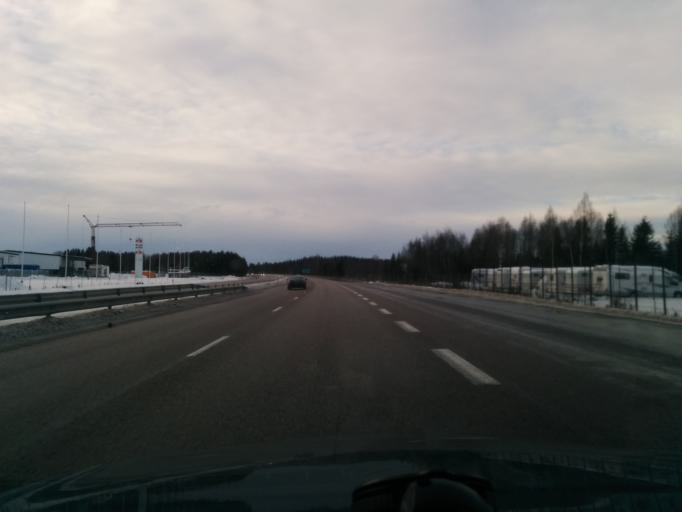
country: SE
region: Uppsala
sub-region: Enkopings Kommun
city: Enkoping
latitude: 59.6493
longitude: 17.1377
